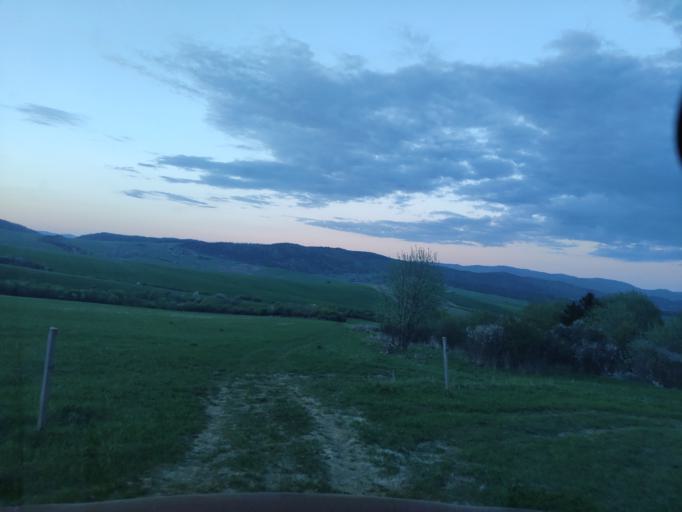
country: SK
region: Presovsky
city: Lipany
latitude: 49.1776
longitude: 20.8108
